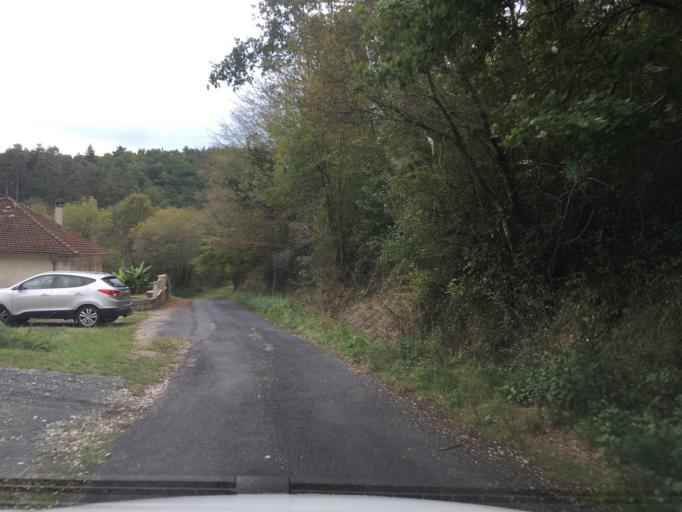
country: FR
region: Limousin
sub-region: Departement de la Correze
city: Brive-la-Gaillarde
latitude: 45.1112
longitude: 1.5483
